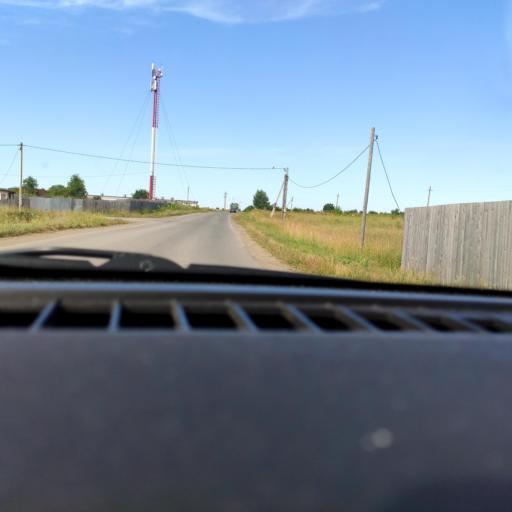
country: RU
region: Perm
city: Polazna
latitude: 58.3531
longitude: 56.2430
